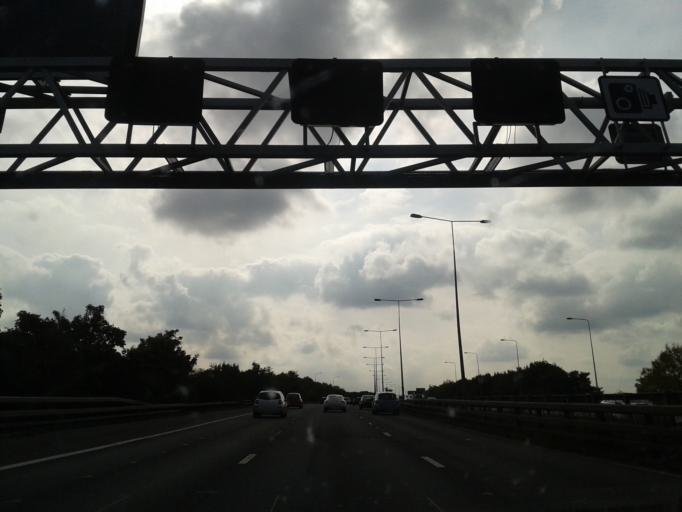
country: GB
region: England
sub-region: Solihull
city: Chelmsley Wood
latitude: 52.4817
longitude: -1.7101
